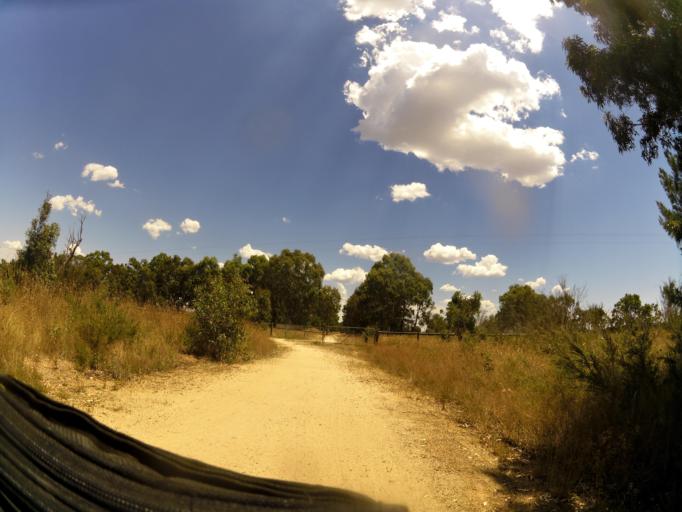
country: AU
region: Victoria
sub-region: Wellington
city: Heyfield
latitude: -37.9805
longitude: 146.8417
